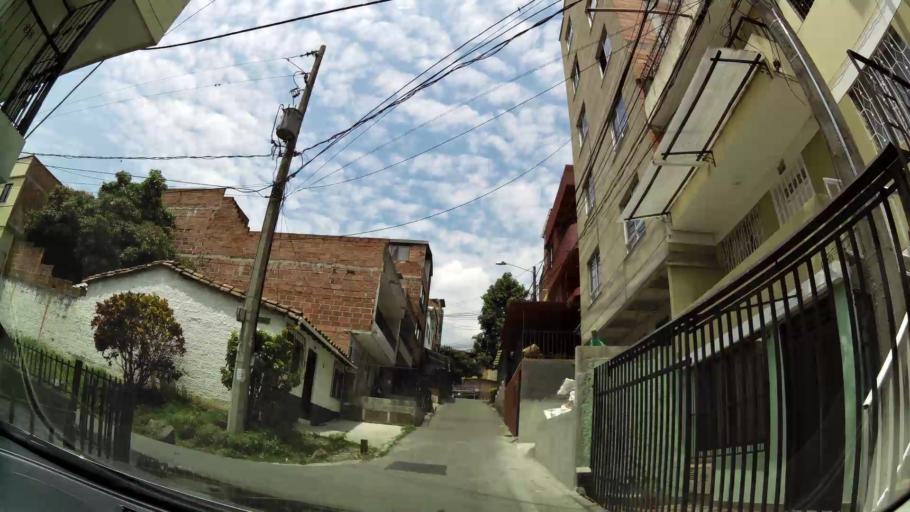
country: CO
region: Antioquia
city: Bello
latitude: 6.3135
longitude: -75.5682
